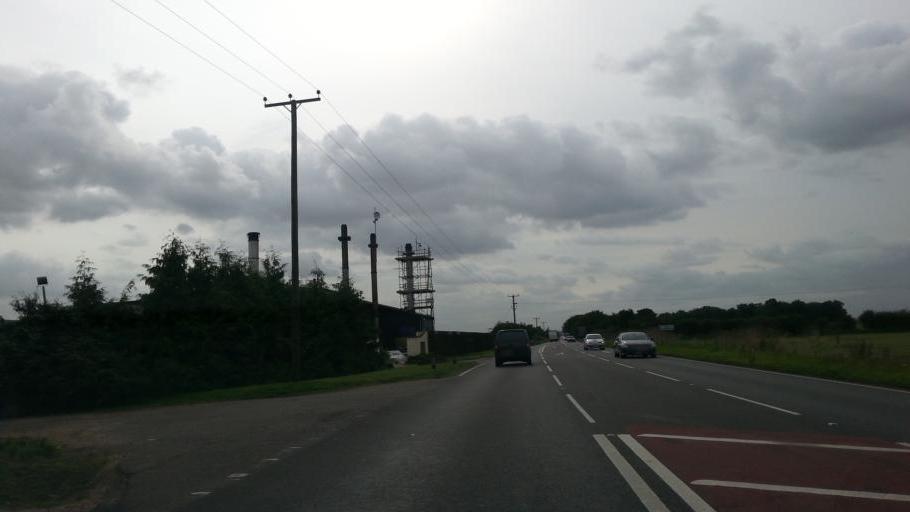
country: GB
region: England
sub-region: Cambridgeshire
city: Duxford
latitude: 52.0827
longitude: 0.1069
